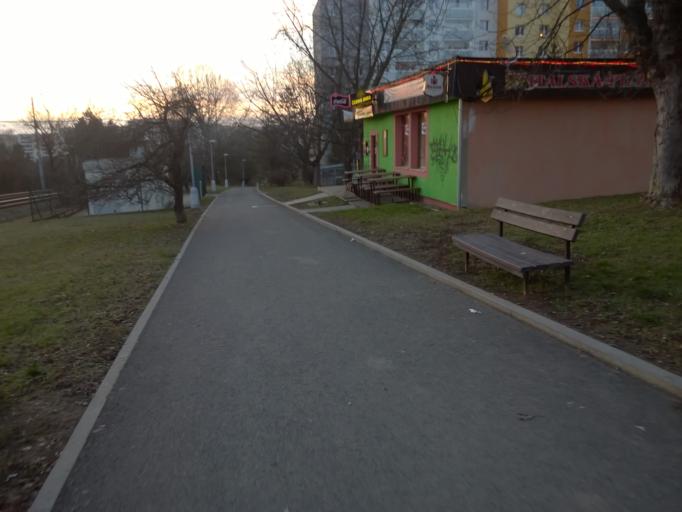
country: CZ
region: South Moravian
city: Ostopovice
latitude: 49.1683
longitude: 16.5617
